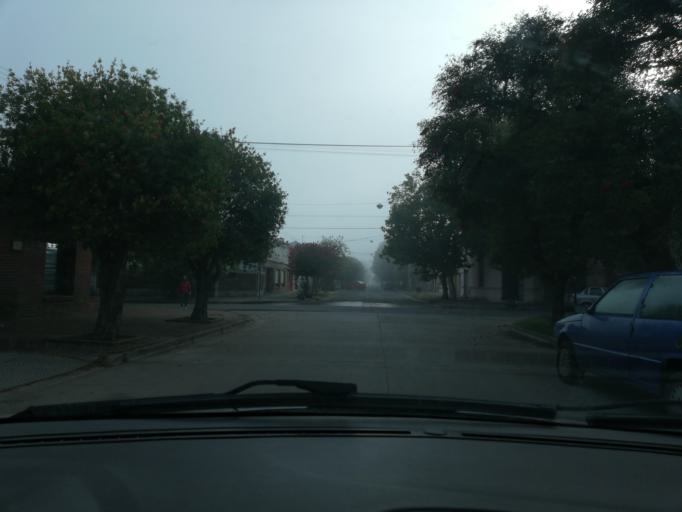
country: AR
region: Buenos Aires
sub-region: Partido de Balcarce
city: Balcarce
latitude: -37.8529
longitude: -58.2613
